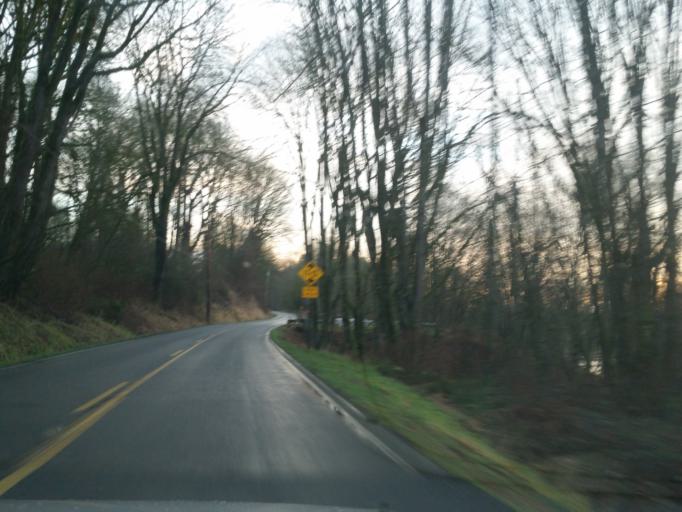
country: US
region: Washington
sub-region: Snohomish County
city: Cathcart
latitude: 47.8591
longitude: -122.0936
